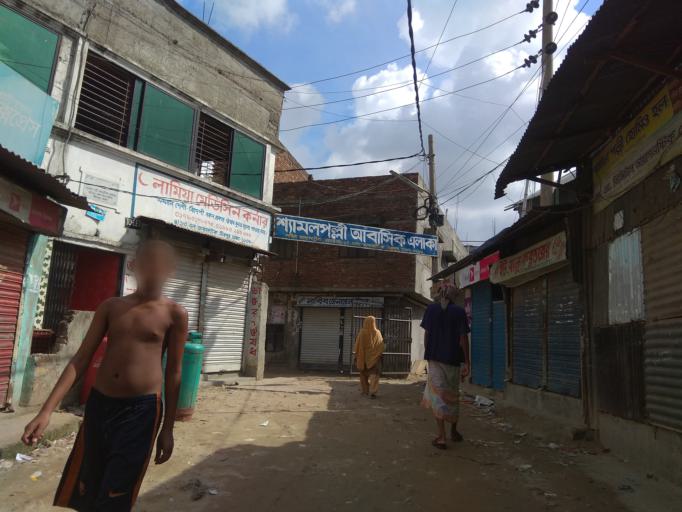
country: BD
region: Dhaka
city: Paltan
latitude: 23.8087
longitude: 90.3850
